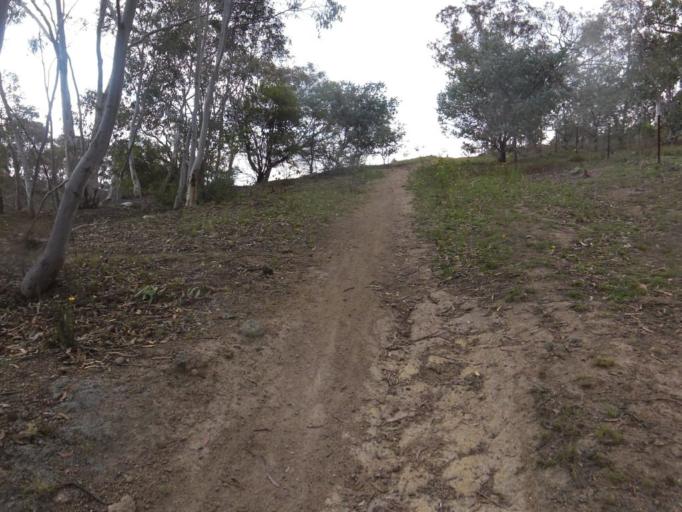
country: AU
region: Australian Capital Territory
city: Forrest
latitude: -35.3481
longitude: 149.1248
